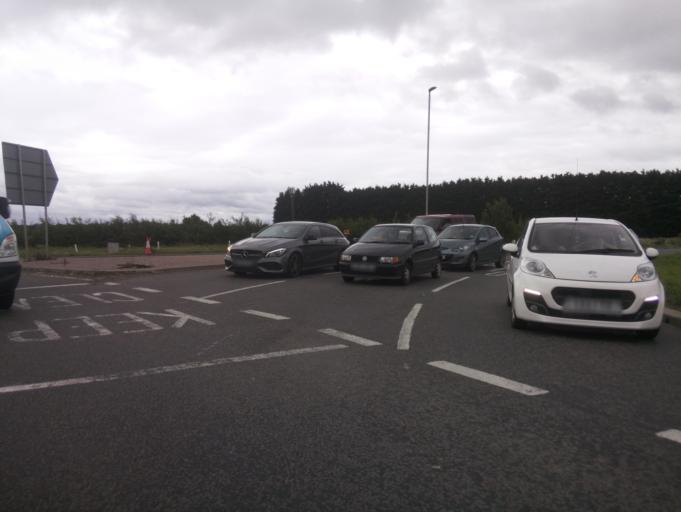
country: GB
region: England
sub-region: Worcestershire
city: Kempsey
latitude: 52.1629
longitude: -2.2159
